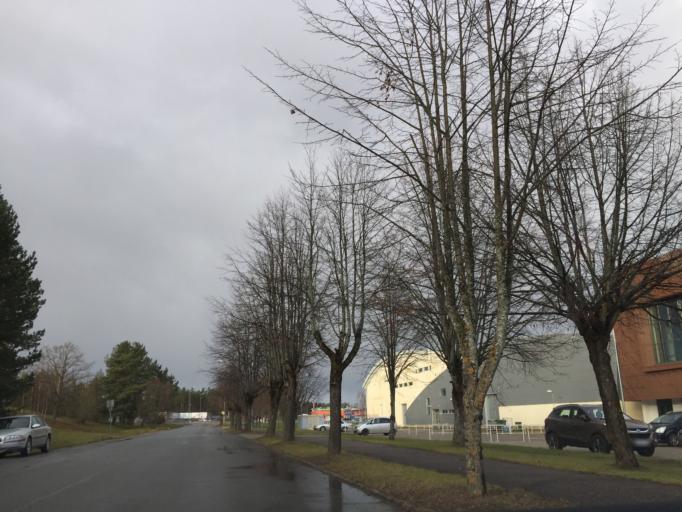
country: LV
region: Valmieras Rajons
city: Valmiera
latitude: 57.5270
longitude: 25.3880
